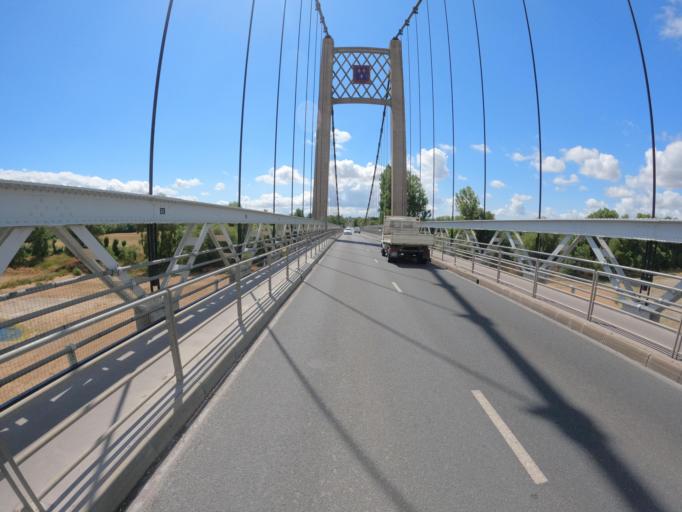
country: FR
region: Pays de la Loire
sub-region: Departement de la Loire-Atlantique
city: Ancenis
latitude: 47.3617
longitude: -1.1763
